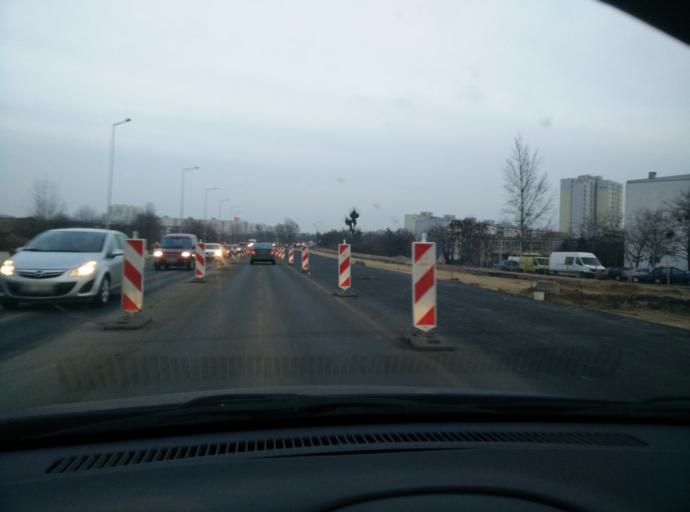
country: PL
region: Greater Poland Voivodeship
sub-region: Poznan
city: Poznan
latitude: 52.3936
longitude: 16.9571
